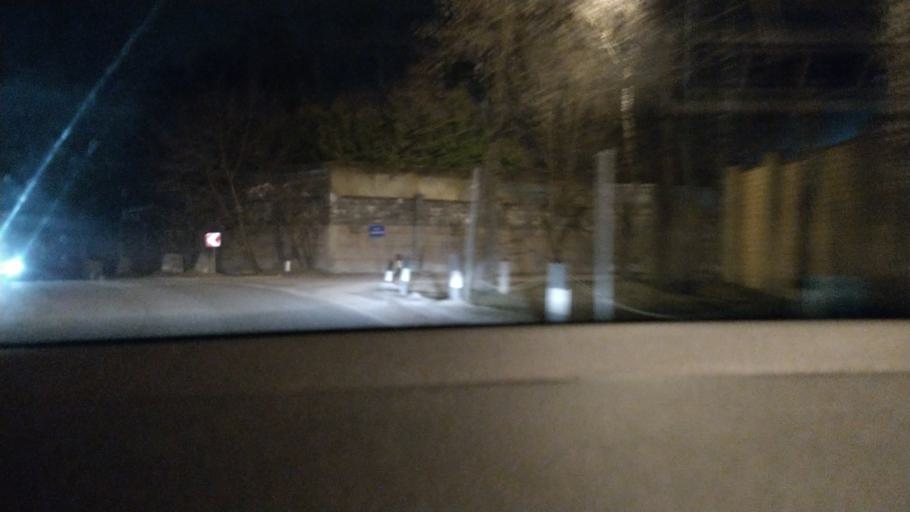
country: RU
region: Moskovskaya
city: Petrovo-Dal'neye
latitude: 55.7222
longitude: 37.2099
